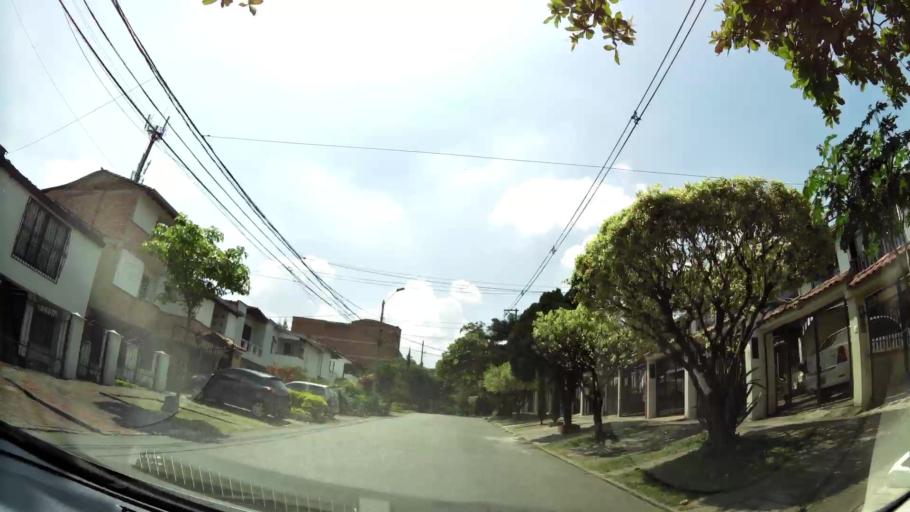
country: CO
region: Antioquia
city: Medellin
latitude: 6.2749
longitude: -75.5804
